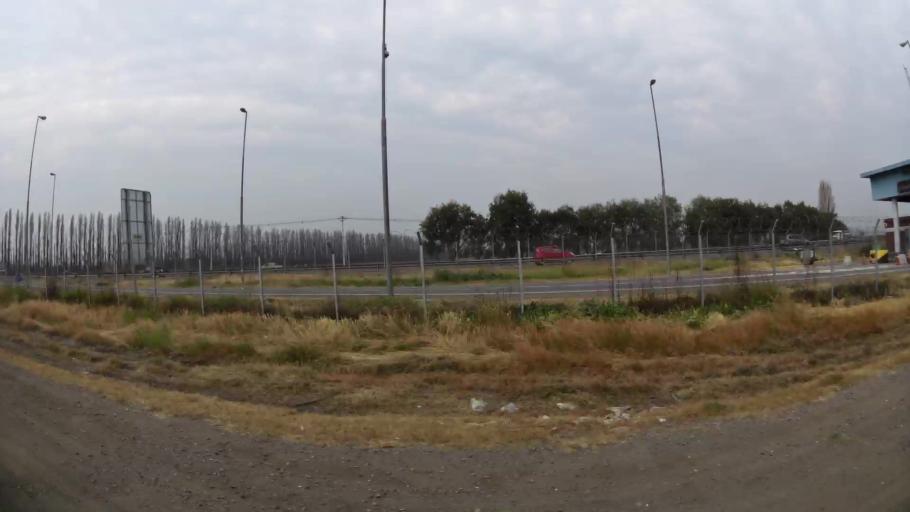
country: CL
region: Santiago Metropolitan
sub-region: Provincia de Chacabuco
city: Chicureo Abajo
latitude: -33.2827
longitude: -70.7028
